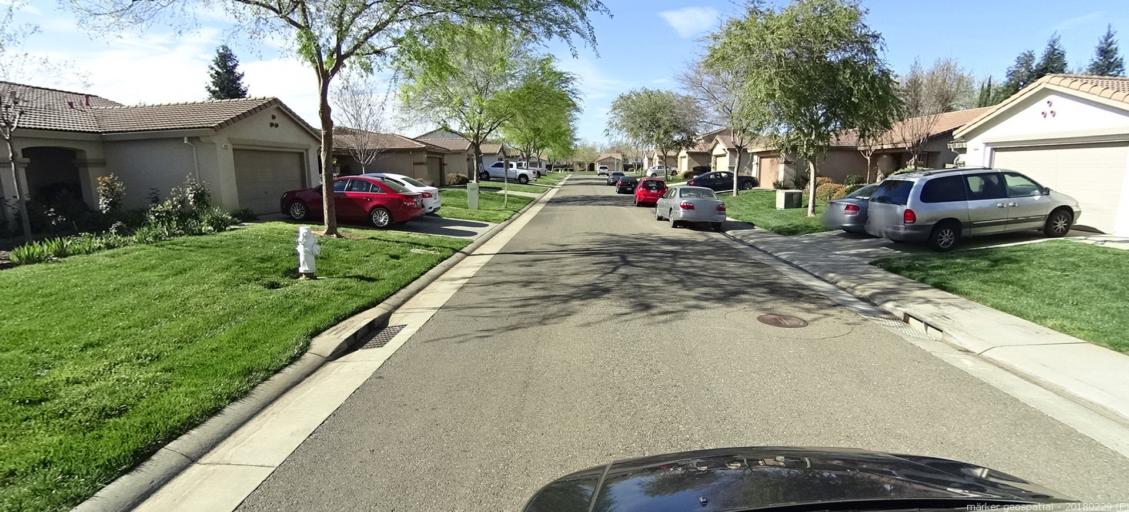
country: US
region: California
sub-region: Sacramento County
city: Rancho Cordova
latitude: 38.5436
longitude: -121.2833
